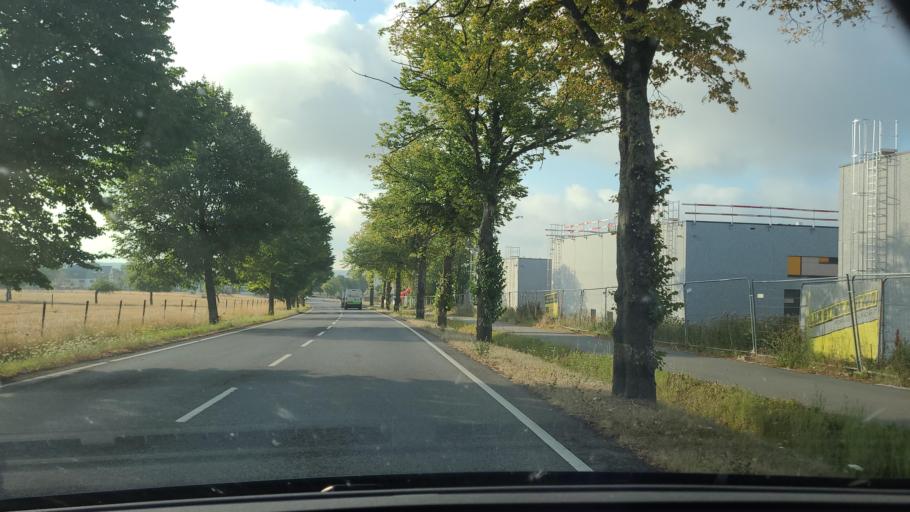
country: LU
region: Luxembourg
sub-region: Canton de Capellen
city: Dippach
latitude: 49.5858
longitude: 5.9727
